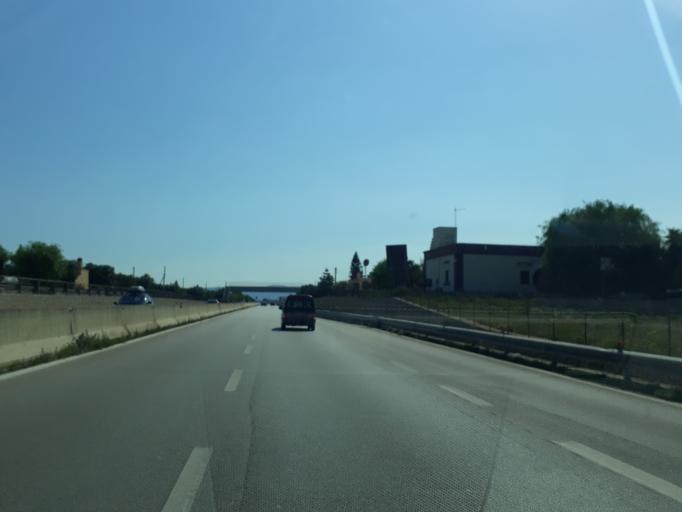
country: IT
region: Apulia
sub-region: Provincia di Brindisi
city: Fasano
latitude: 40.8706
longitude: 17.3432
